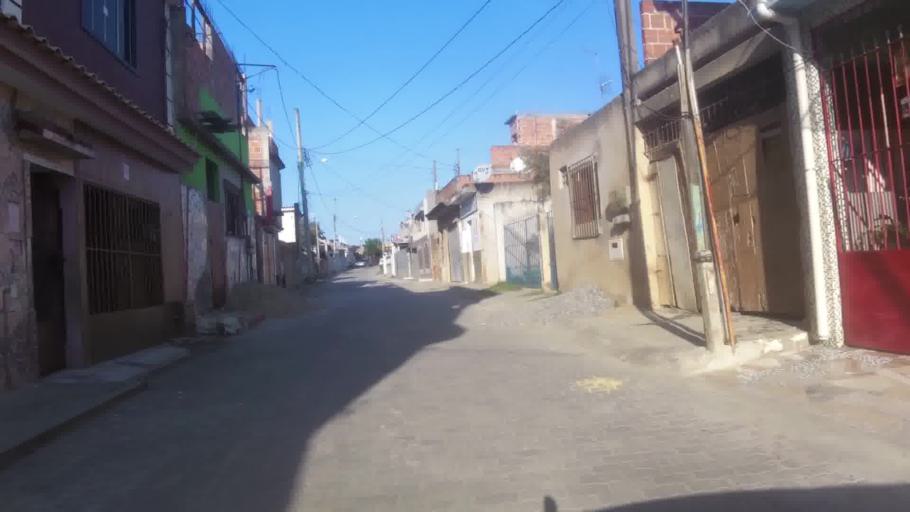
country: BR
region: Espirito Santo
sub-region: Itapemirim
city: Itapemirim
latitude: -21.0182
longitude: -40.8163
